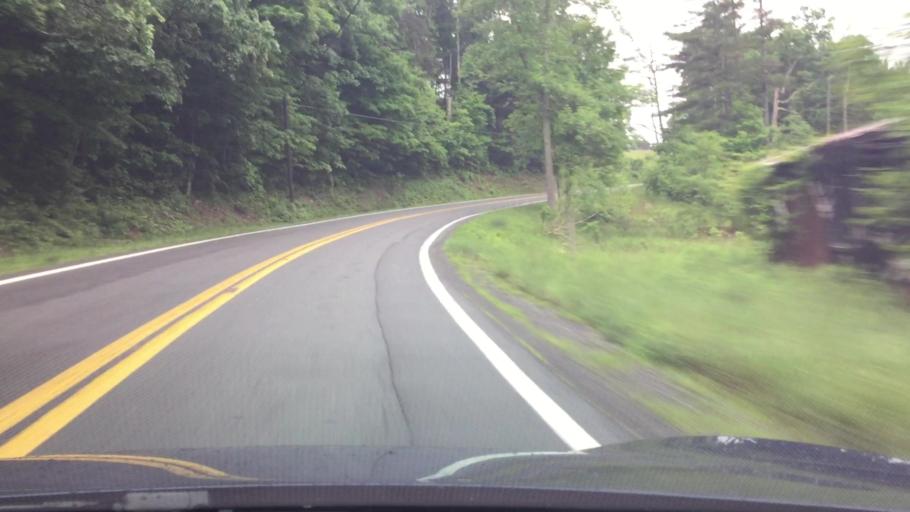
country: US
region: West Virginia
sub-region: Summers County
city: Hinton
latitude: 37.5760
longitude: -80.7871
